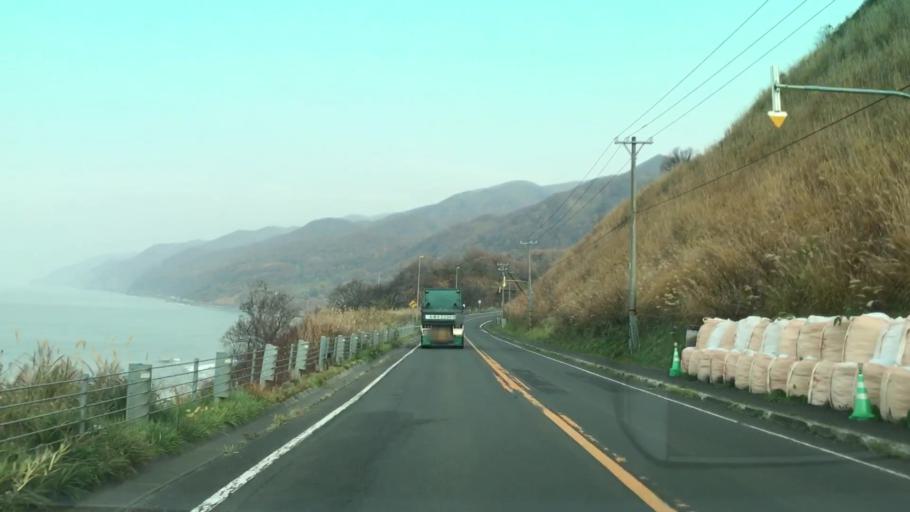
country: JP
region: Hokkaido
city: Ishikari
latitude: 43.4092
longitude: 141.4303
